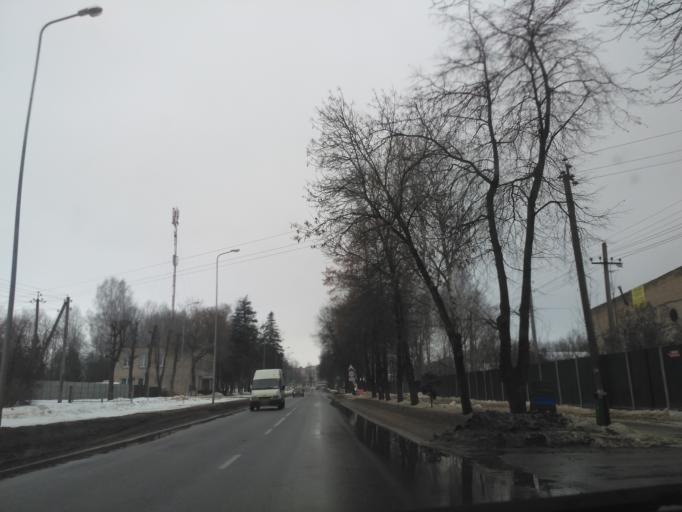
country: BY
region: Minsk
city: Horad Zhodzina
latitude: 54.0953
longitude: 28.3350
